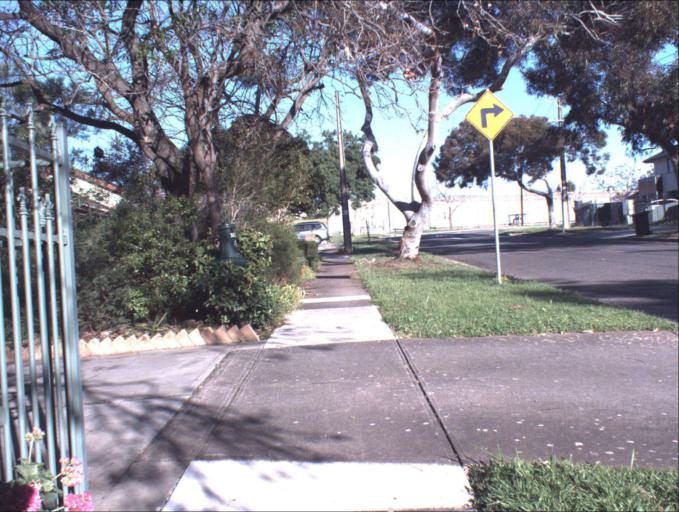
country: AU
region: South Australia
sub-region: Salisbury
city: Ingle Farm
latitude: -34.8427
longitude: 138.6261
